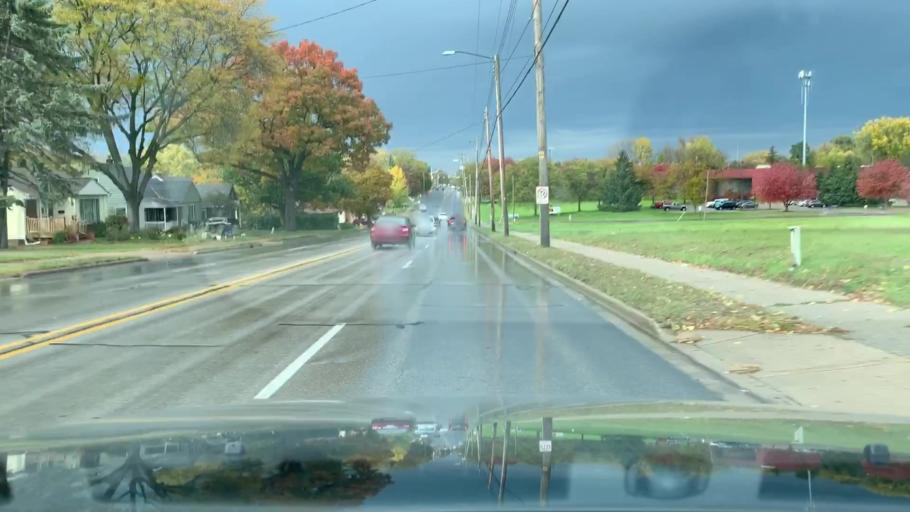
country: US
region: Michigan
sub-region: Kent County
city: Grand Rapids
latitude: 42.9796
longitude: -85.6398
